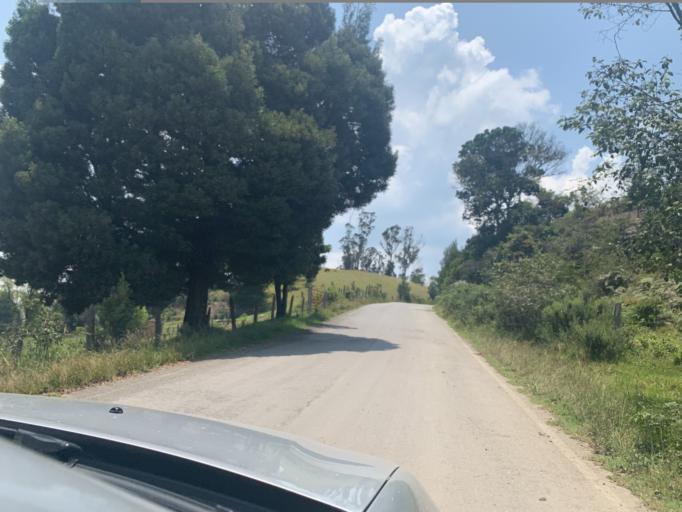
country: CO
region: Boyaca
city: Chiquinquira
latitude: 5.5768
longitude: -73.7469
